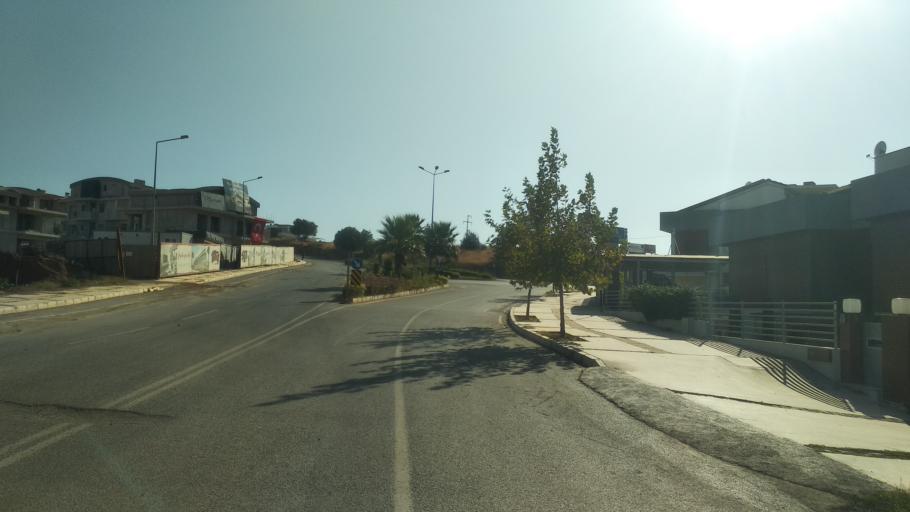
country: TR
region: Izmir
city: Urla
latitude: 38.3556
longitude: 26.8710
